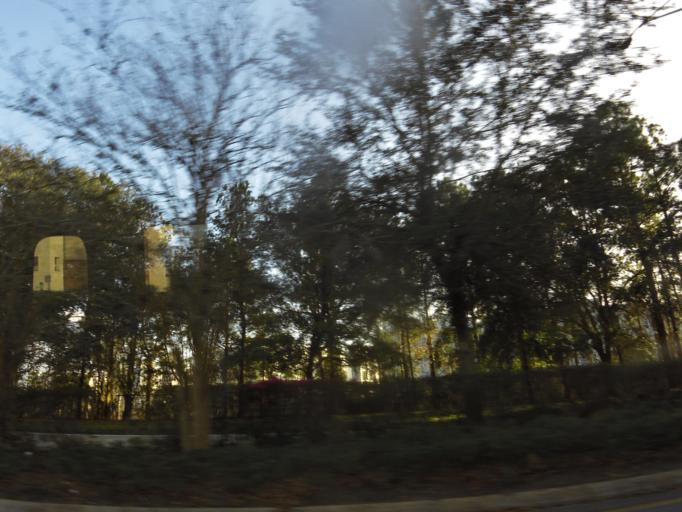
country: US
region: Florida
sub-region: Duval County
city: Jacksonville
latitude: 30.2544
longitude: -81.5505
